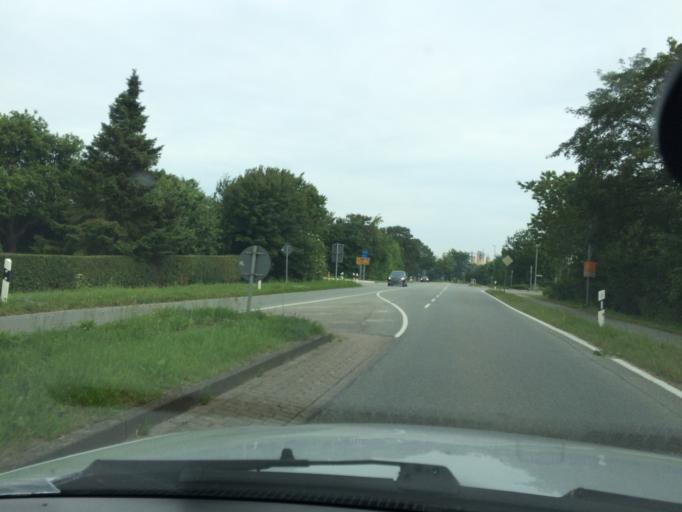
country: DE
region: Schleswig-Holstein
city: Jarplund-Weding
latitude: 54.7366
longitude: 9.4415
